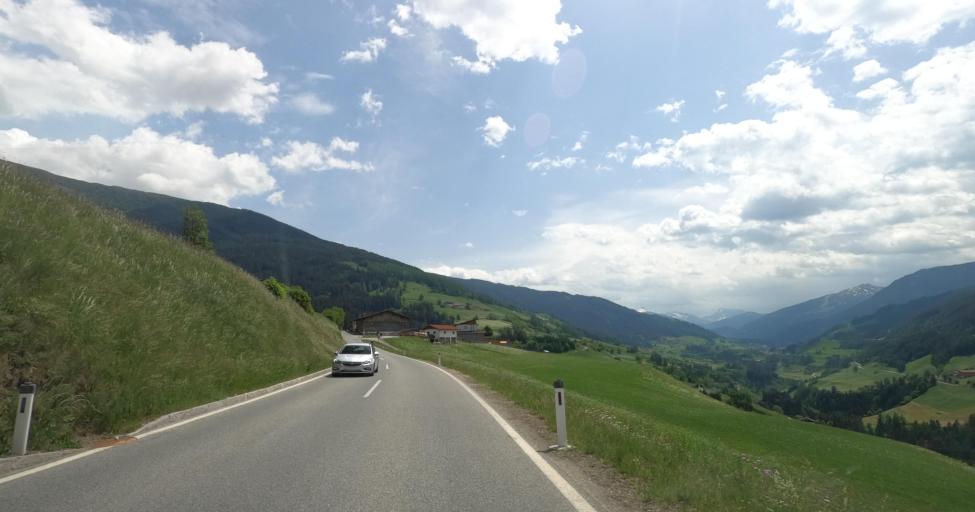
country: AT
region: Tyrol
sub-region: Politischer Bezirk Innsbruck Land
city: Ellbogen
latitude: 47.1661
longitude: 11.4474
